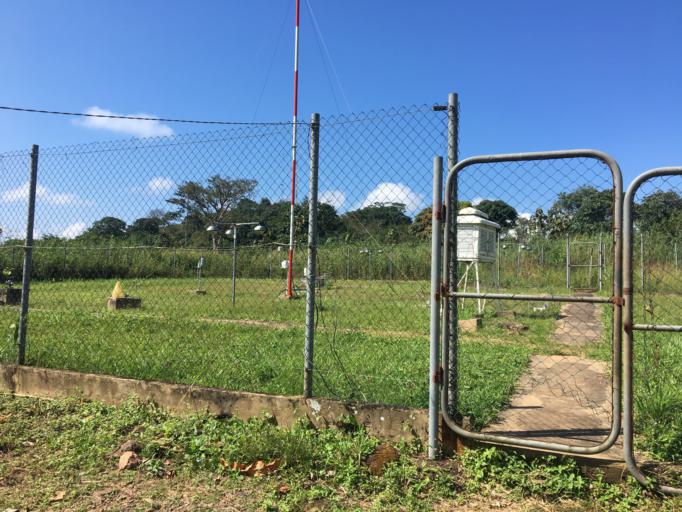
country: TG
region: Plateaux
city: Kpalime
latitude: 6.9563
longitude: 0.5721
